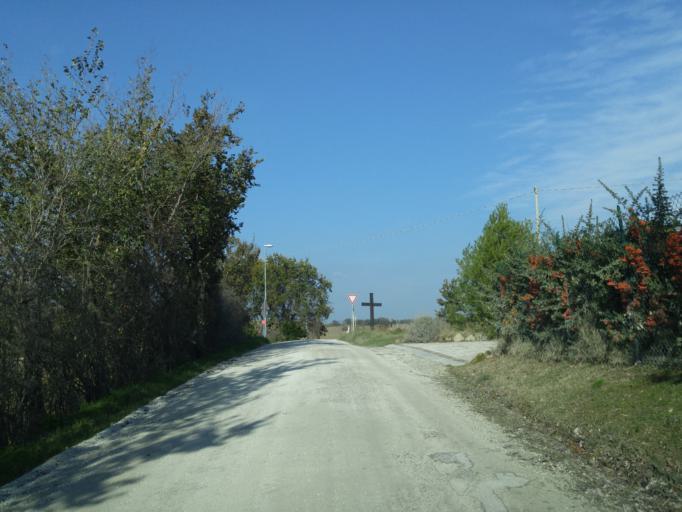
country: IT
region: The Marches
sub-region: Provincia di Pesaro e Urbino
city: Lucrezia
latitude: 43.7945
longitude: 12.9239
